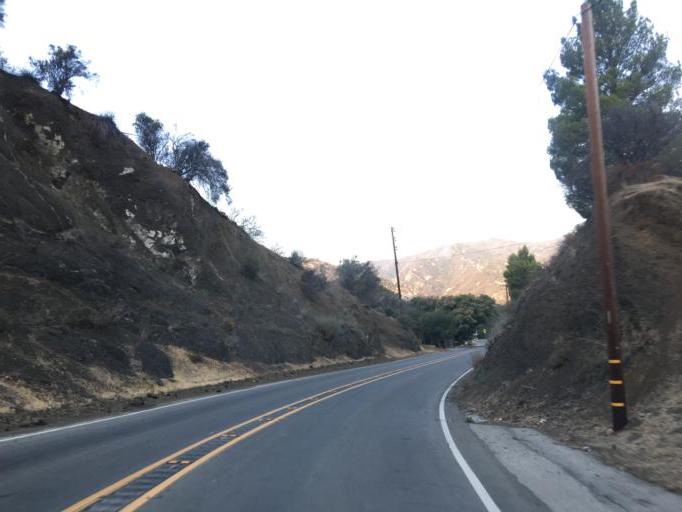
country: US
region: California
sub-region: Los Angeles County
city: Malibu Beach
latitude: 34.0837
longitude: -118.6826
